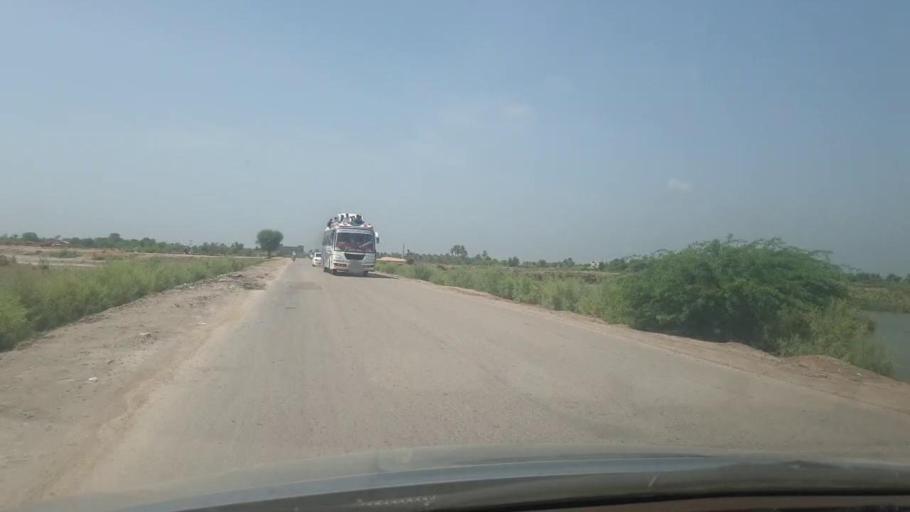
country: PK
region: Sindh
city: Bozdar
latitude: 27.2312
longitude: 68.5691
